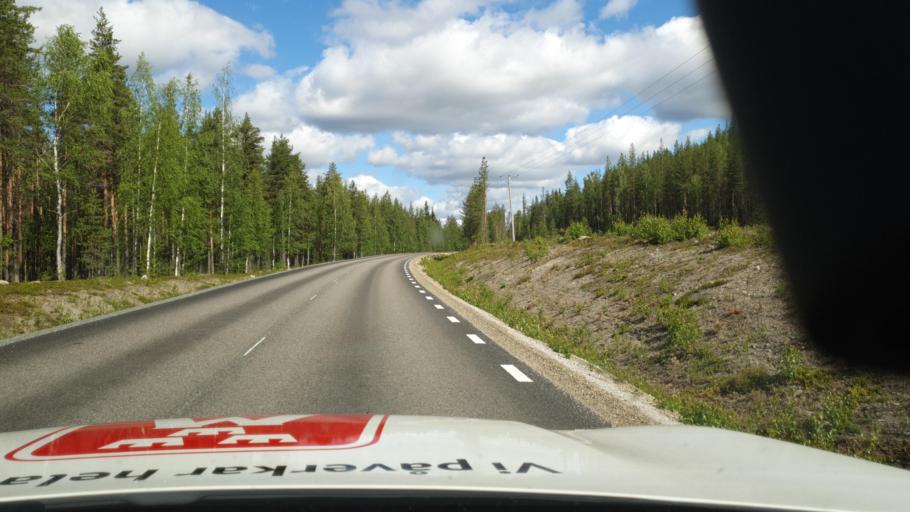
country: SE
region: Vaesterbotten
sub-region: Lycksele Kommun
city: Lycksele
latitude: 64.8628
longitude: 18.7217
